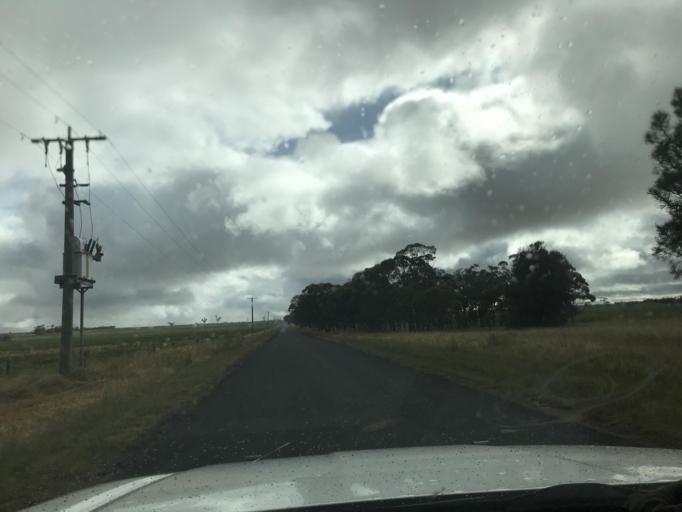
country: AU
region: South Australia
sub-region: Tatiara
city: Bordertown
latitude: -36.3613
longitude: 141.2646
